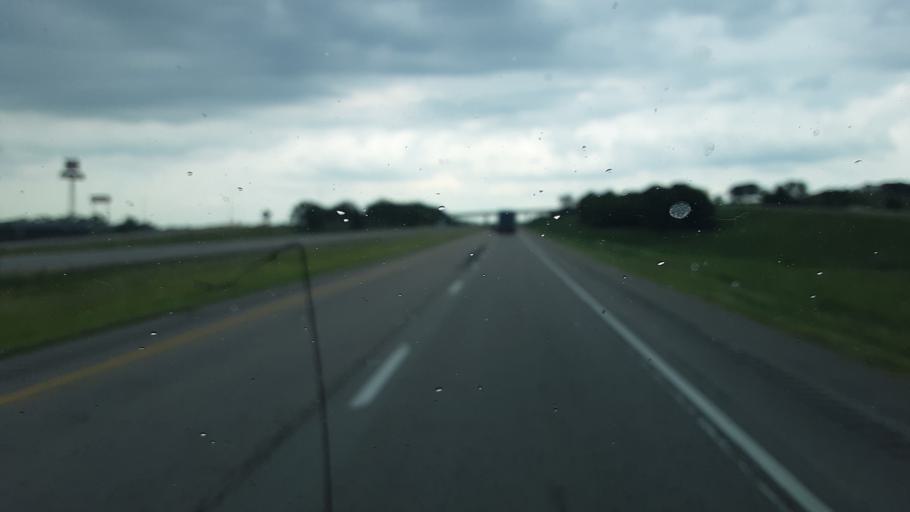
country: US
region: Iowa
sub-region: Pottawattamie County
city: Council Bluffs
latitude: 41.3730
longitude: -95.6787
